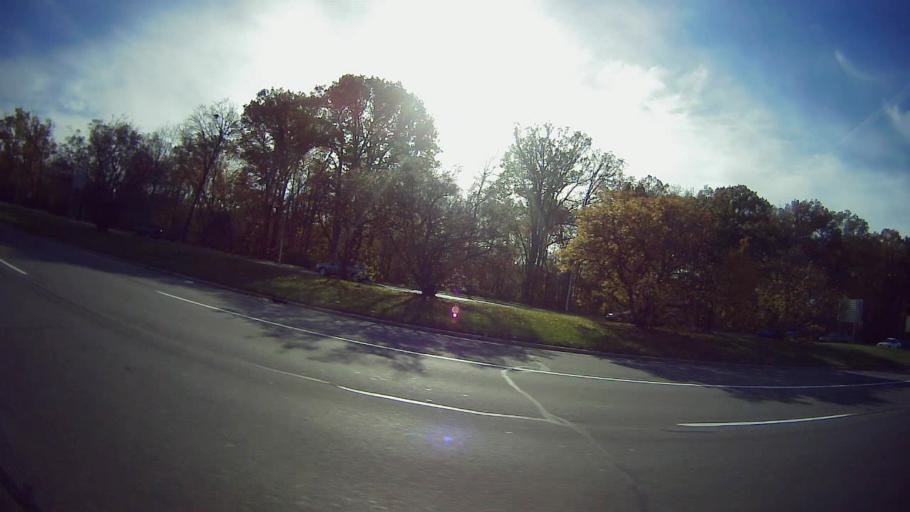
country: US
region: Michigan
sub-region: Wayne County
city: Dearborn Heights
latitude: 42.3289
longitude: -83.2265
